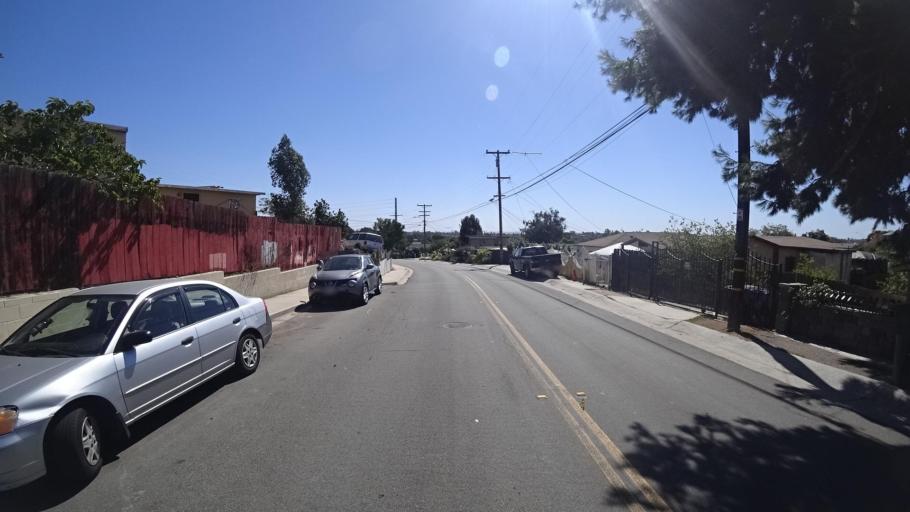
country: US
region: California
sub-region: San Diego County
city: National City
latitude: 32.6642
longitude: -117.0807
